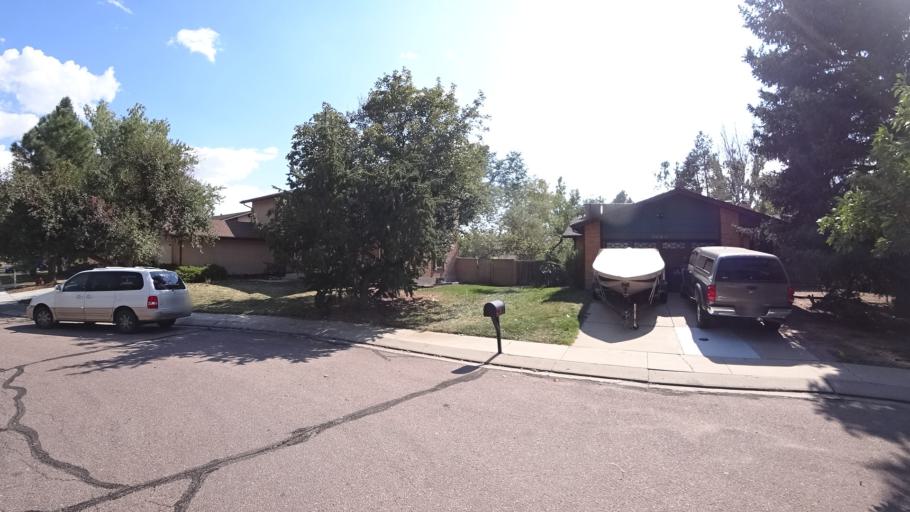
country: US
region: Colorado
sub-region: El Paso County
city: Cimarron Hills
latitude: 38.8715
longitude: -104.7546
